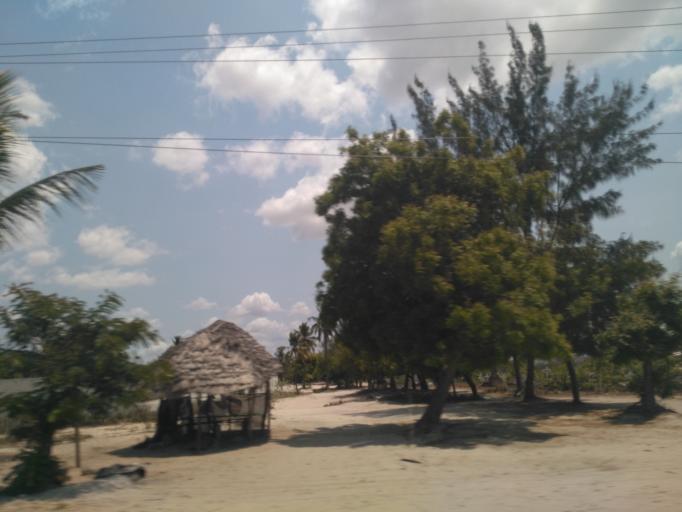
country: TZ
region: Dar es Salaam
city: Dar es Salaam
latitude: -6.8255
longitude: 39.3268
